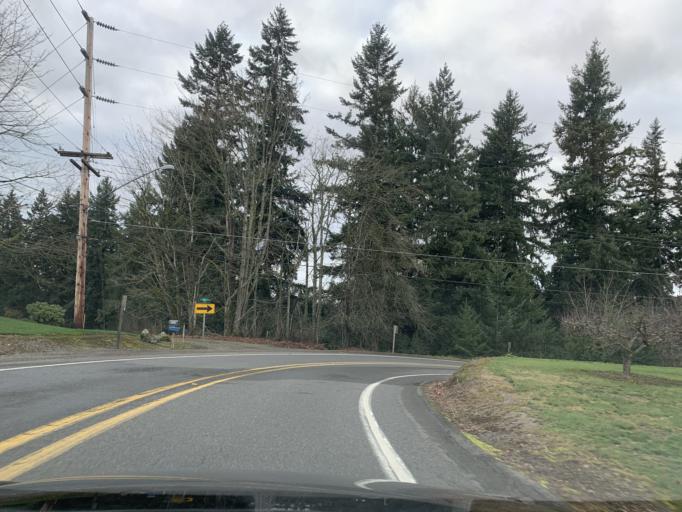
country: US
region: Washington
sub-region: Pierce County
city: Milton
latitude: 47.2356
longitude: -122.3069
